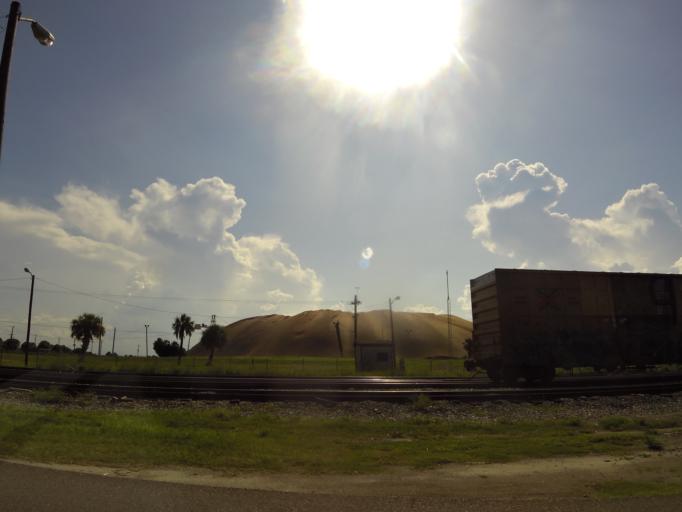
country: US
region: Florida
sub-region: Nassau County
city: Fernandina Beach
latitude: 30.6636
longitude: -81.4642
